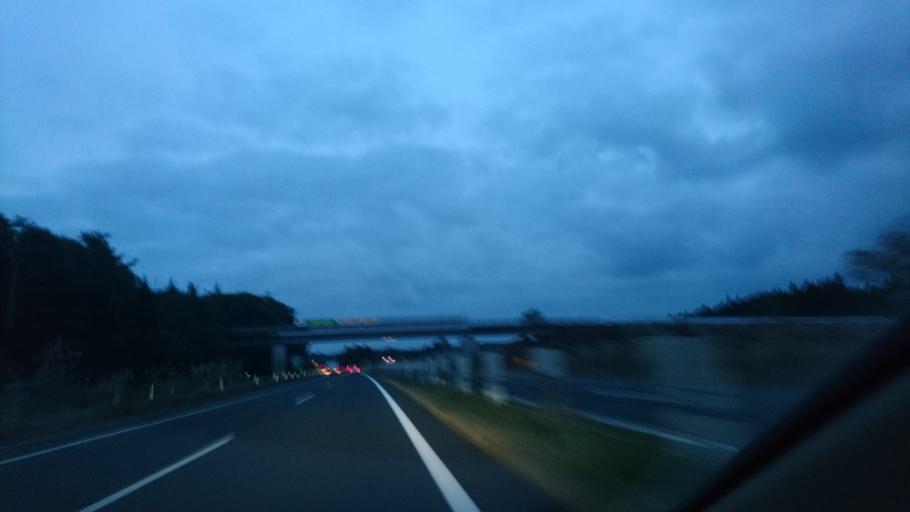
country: JP
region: Iwate
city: Hanamaki
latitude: 39.5100
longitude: 141.1018
